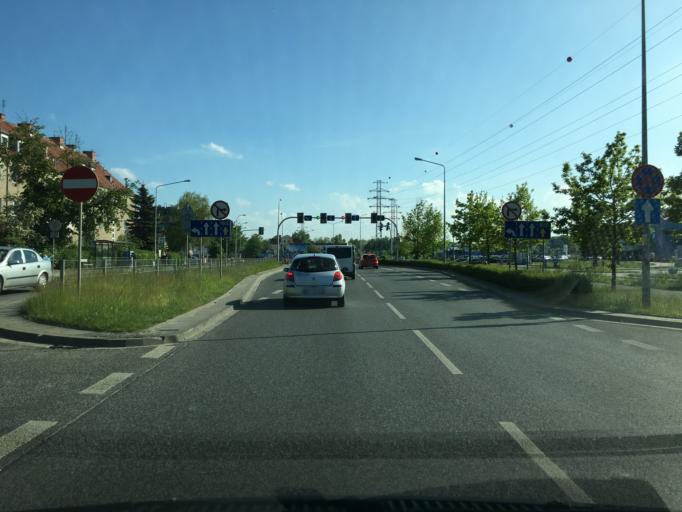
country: PL
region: Lower Silesian Voivodeship
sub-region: Powiat wroclawski
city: Wroclaw
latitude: 51.0759
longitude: 17.0330
